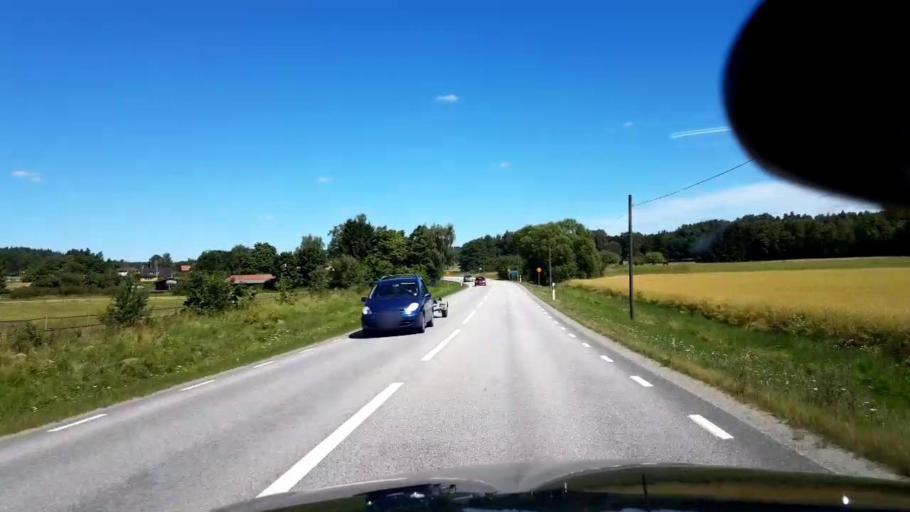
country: SE
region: Uppsala
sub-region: Habo Kommun
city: Balsta
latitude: 59.6372
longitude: 17.6077
